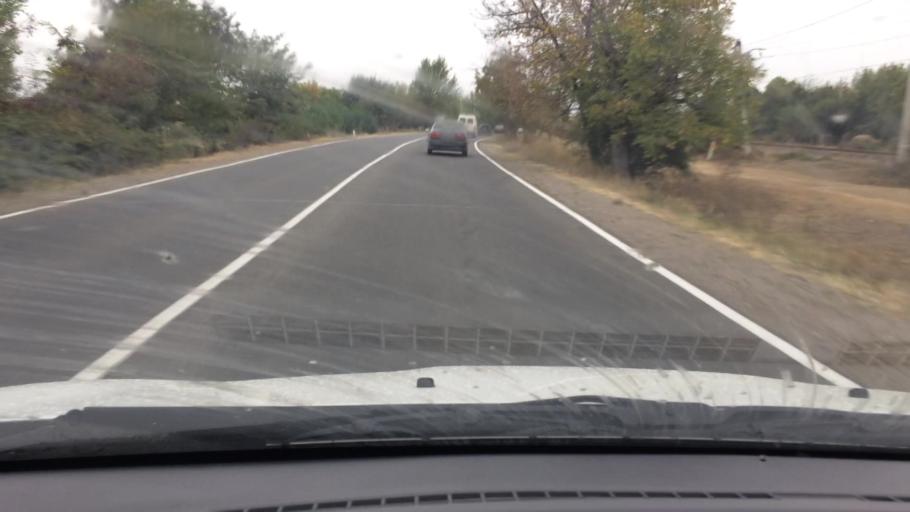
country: GE
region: Kvemo Kartli
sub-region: Marneuli
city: Marneuli
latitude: 41.4151
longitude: 44.8273
